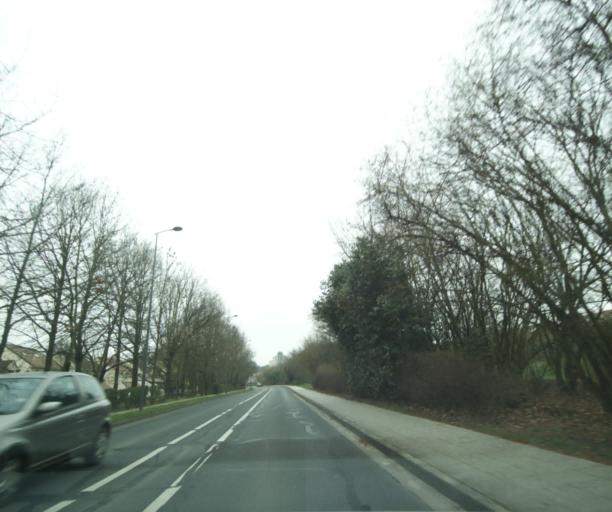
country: FR
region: Ile-de-France
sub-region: Departement du Val-d'Oise
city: Courdimanche
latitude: 49.0426
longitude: 2.0121
